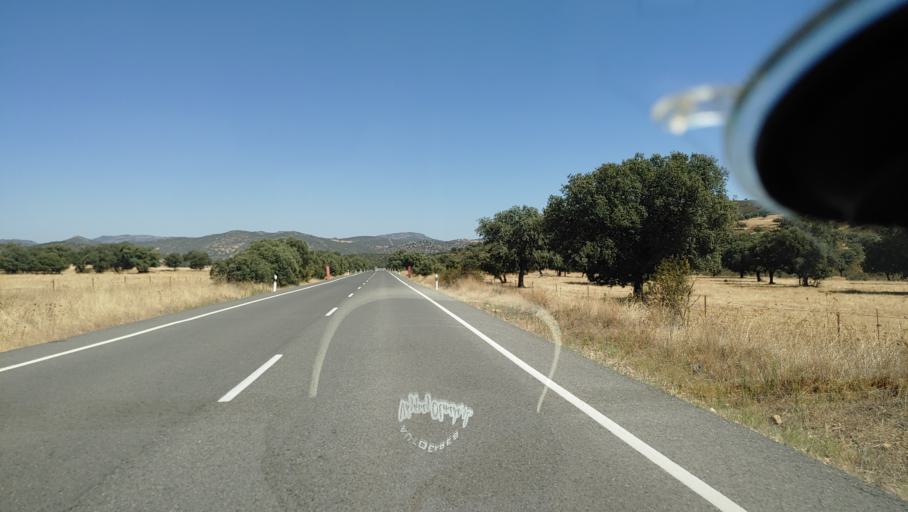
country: ES
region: Andalusia
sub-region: Province of Cordoba
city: Santa Eufemia
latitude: 38.6714
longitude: -4.9203
